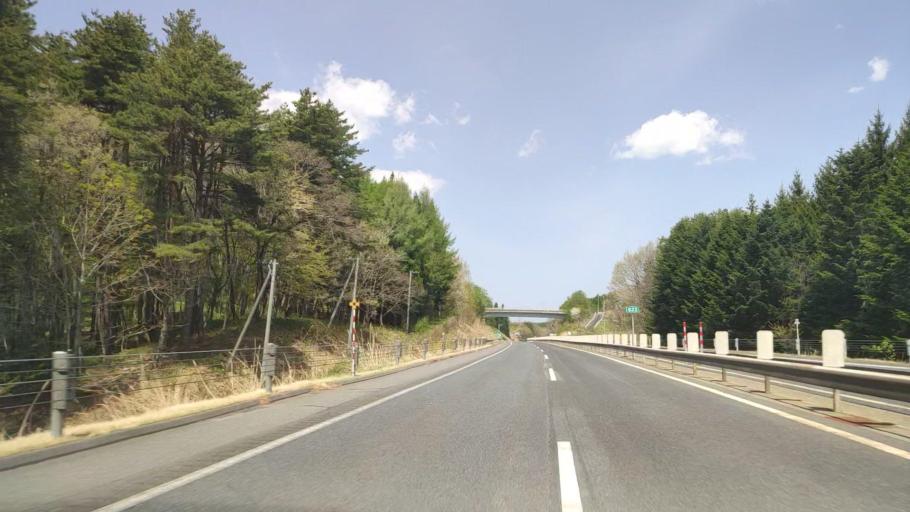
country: JP
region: Aomori
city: Hachinohe
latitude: 40.4140
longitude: 141.4429
